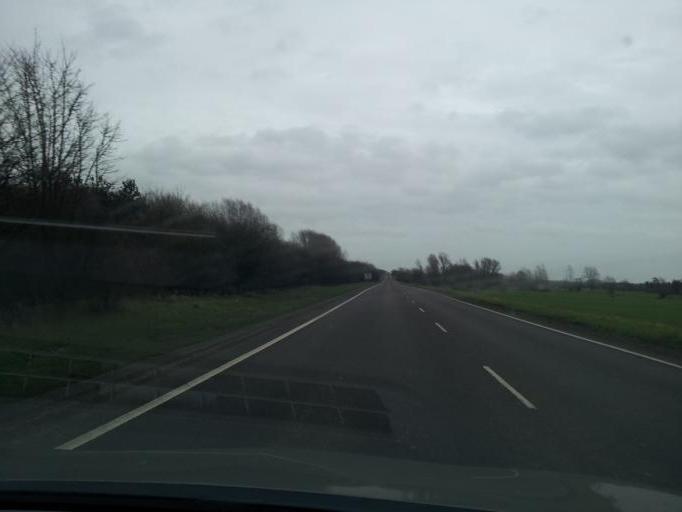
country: GB
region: England
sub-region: Norfolk
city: Diss
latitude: 52.3625
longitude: 1.1546
